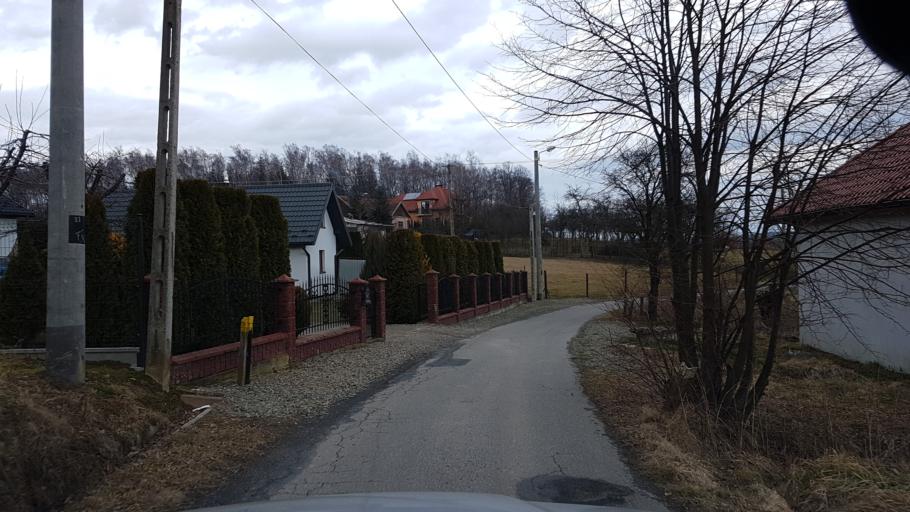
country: PL
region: Lesser Poland Voivodeship
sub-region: Powiat nowosadecki
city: Stary Sacz
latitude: 49.5282
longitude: 20.6233
